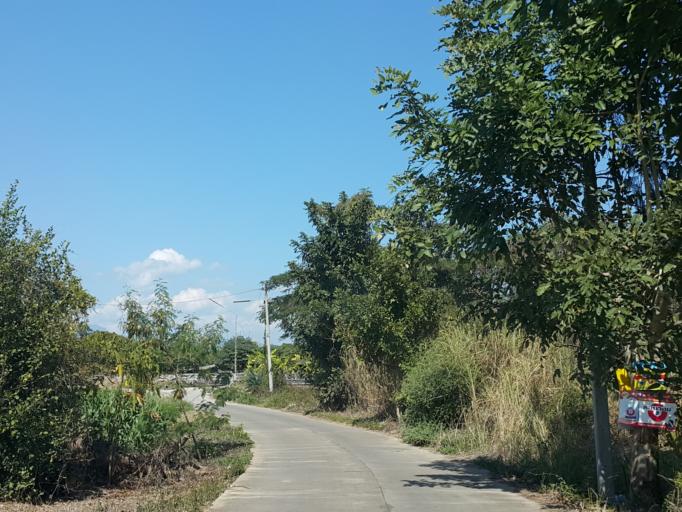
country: TH
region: Chiang Mai
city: Mae Taeng
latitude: 19.0972
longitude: 98.9401
